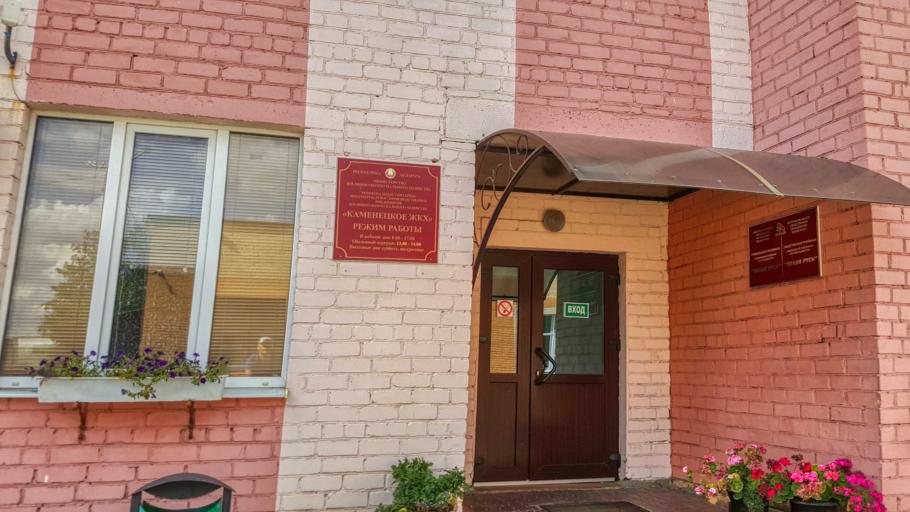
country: BY
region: Brest
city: Kamyanyets
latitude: 52.3989
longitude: 23.8317
